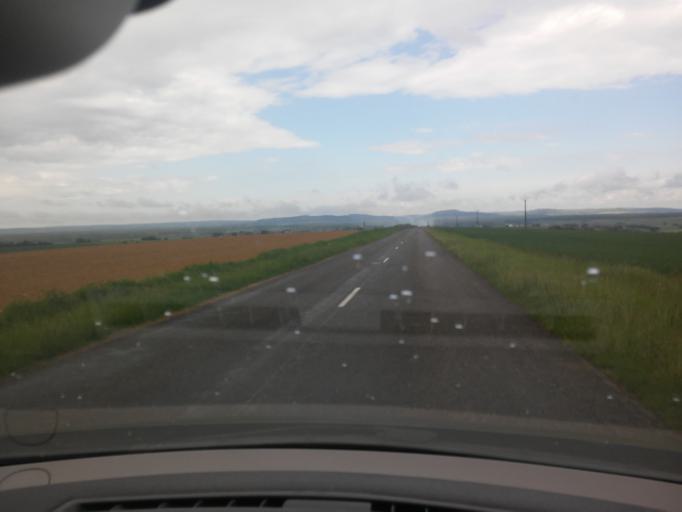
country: FR
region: Lorraine
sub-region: Departement de Meurthe-et-Moselle
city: Longuyon
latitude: 49.3663
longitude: 5.5509
